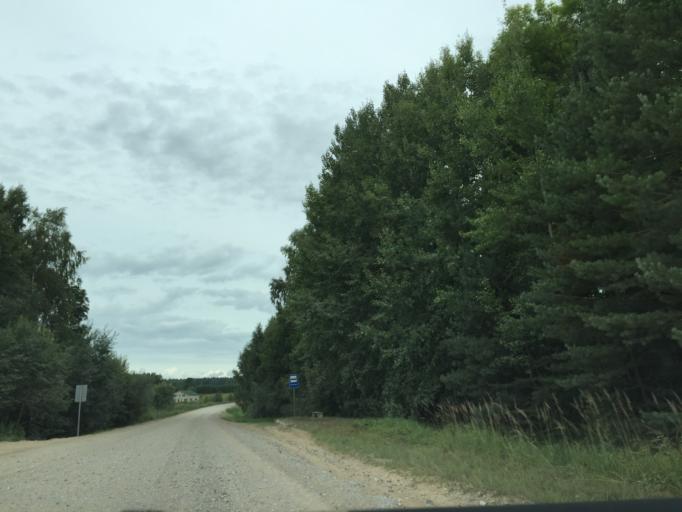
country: LV
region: Jaunpils
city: Jaunpils
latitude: 56.7234
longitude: 23.1469
